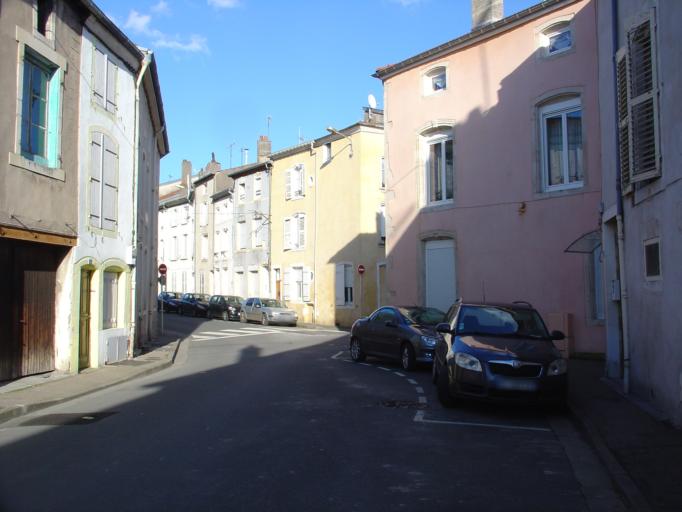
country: FR
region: Lorraine
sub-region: Departement de Meurthe-et-Moselle
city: Toul
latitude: 48.6777
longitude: 5.8902
